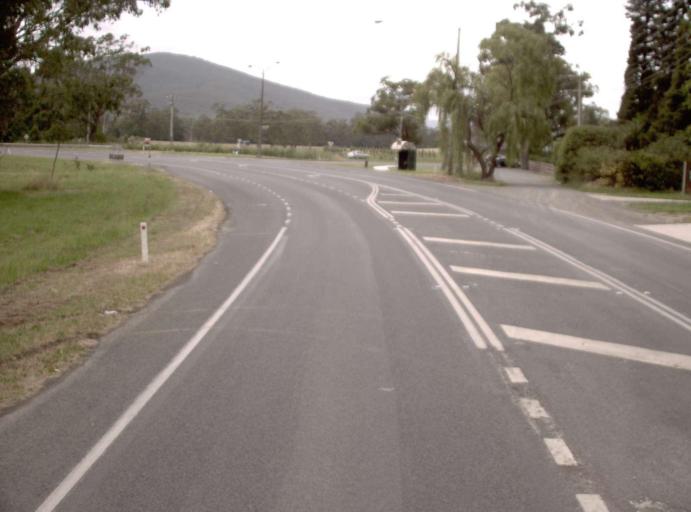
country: AU
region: Victoria
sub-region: Yarra Ranges
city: Yarra Junction
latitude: -37.7832
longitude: 145.6251
